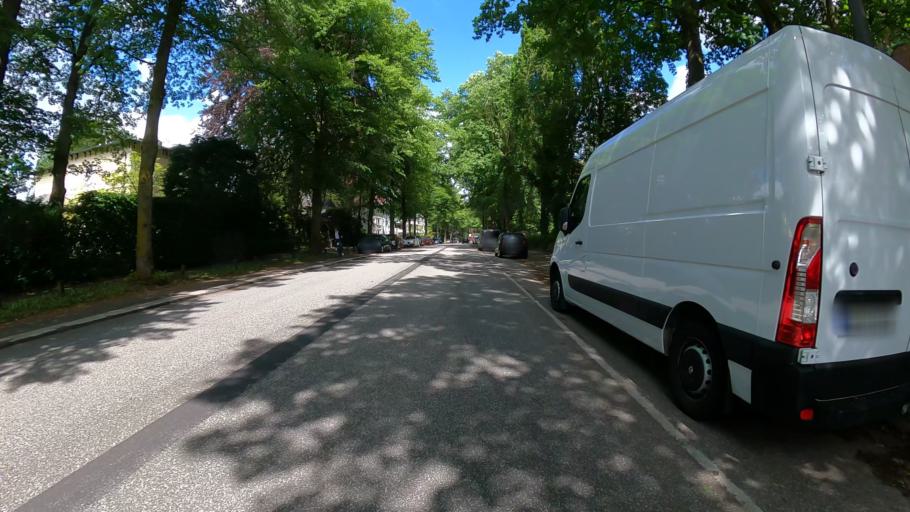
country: DE
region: Hamburg
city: Alsterdorf
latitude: 53.6114
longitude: 10.0134
